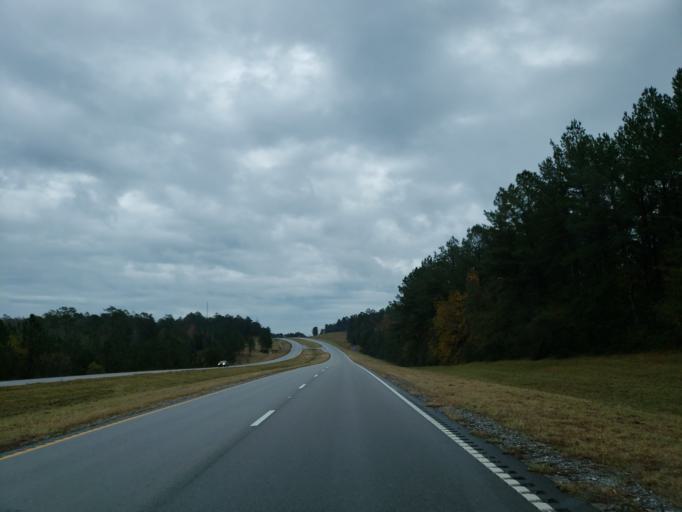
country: US
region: Mississippi
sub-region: Wayne County
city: Waynesboro
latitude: 31.6869
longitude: -88.7039
